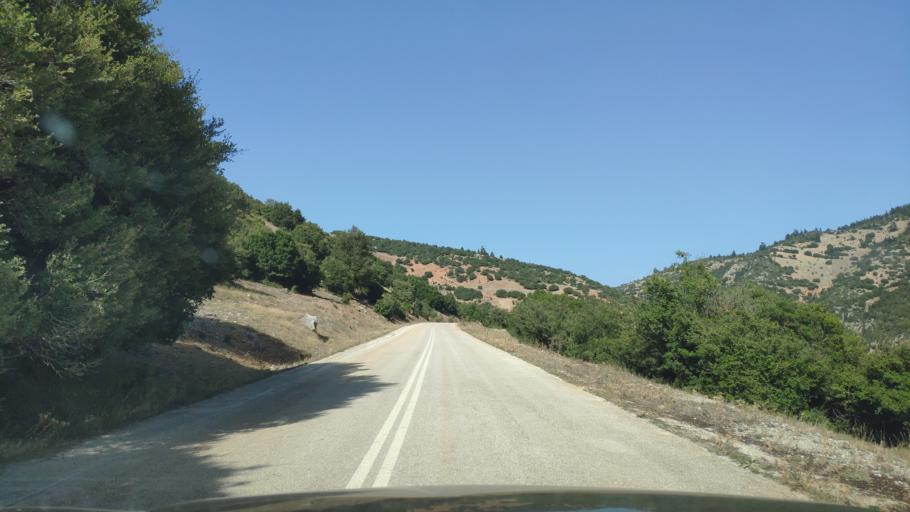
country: GR
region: West Greece
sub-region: Nomos Achaias
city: Aiyira
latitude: 37.9667
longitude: 22.3474
